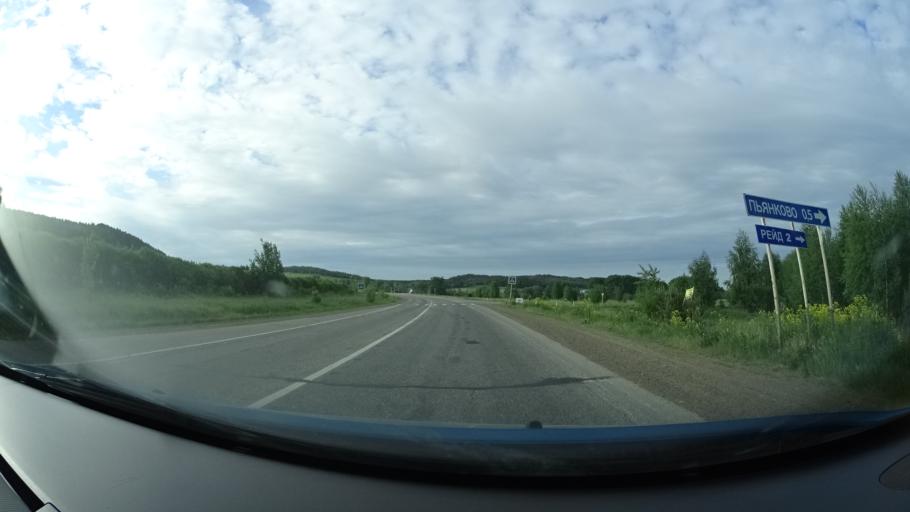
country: RU
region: Perm
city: Osa
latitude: 57.3332
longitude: 55.5841
